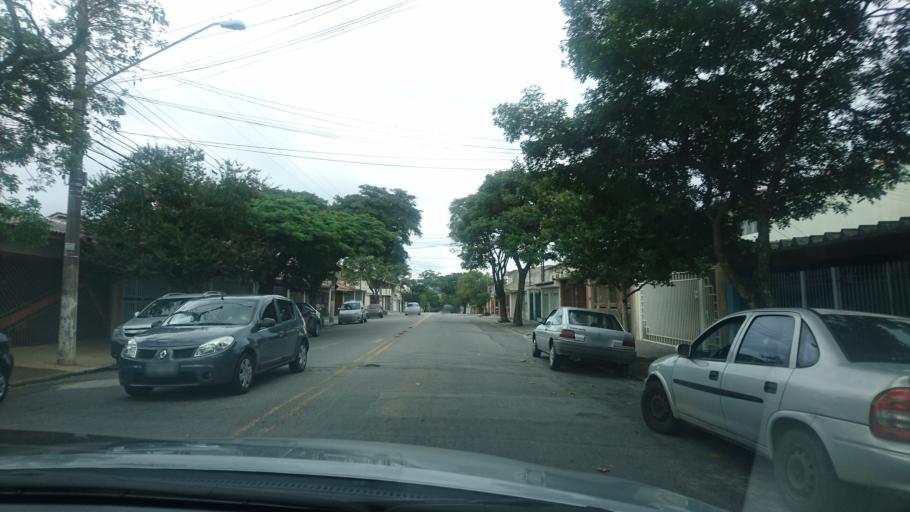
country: BR
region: Sao Paulo
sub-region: Guarulhos
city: Guarulhos
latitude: -23.4526
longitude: -46.5275
